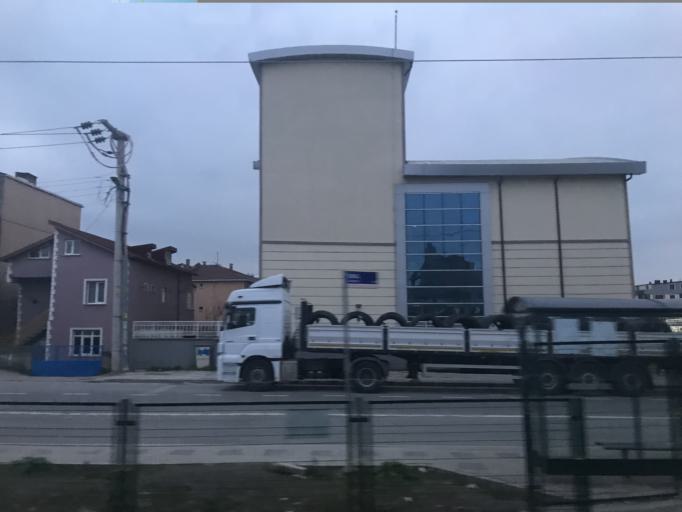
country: TR
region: Kocaeli
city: Darica
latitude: 40.7870
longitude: 29.4008
